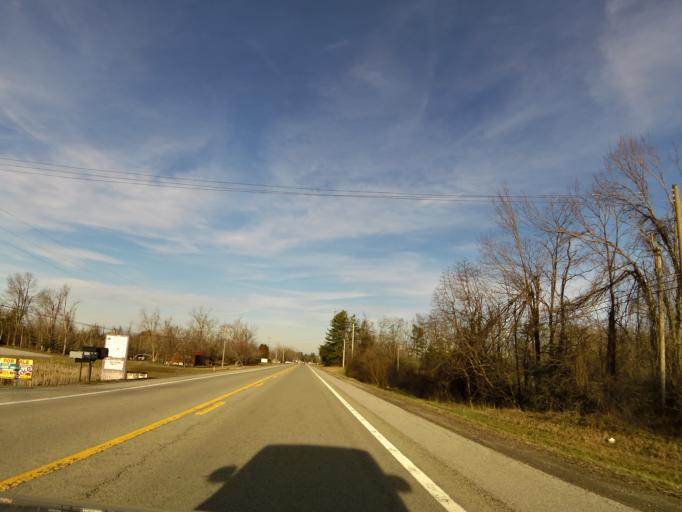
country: US
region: Tennessee
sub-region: Cumberland County
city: Crossville
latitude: 35.9735
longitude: -85.1839
